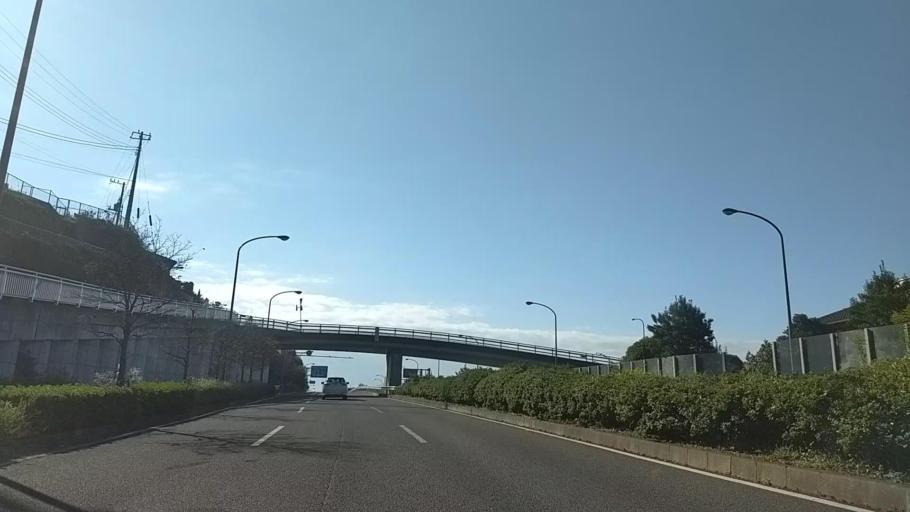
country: JP
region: Kanagawa
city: Yokohama
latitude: 35.4599
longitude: 139.5628
